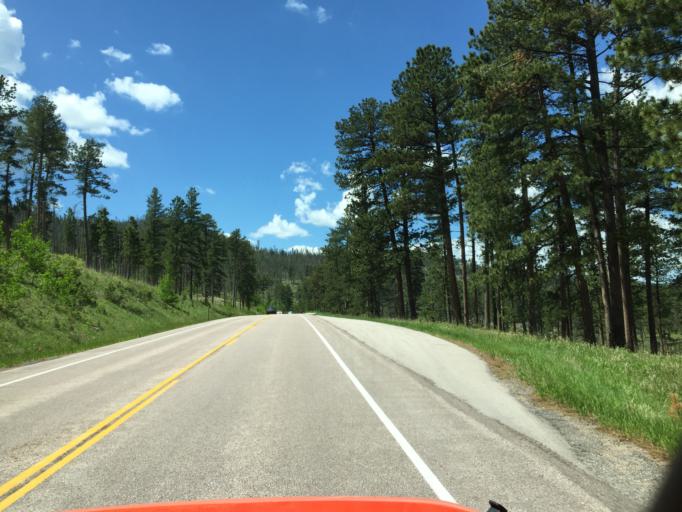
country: US
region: South Dakota
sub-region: Custer County
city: Custer
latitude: 43.8976
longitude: -103.5088
